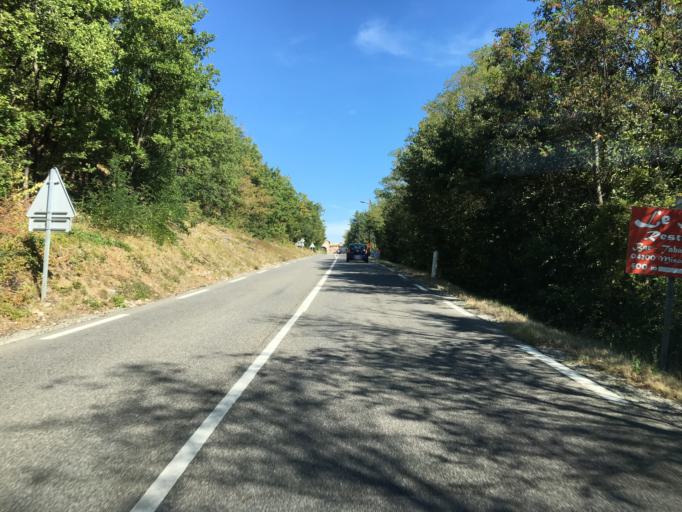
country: FR
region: Provence-Alpes-Cote d'Azur
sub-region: Departement des Hautes-Alpes
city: Laragne-Monteglin
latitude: 44.2637
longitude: 5.8613
